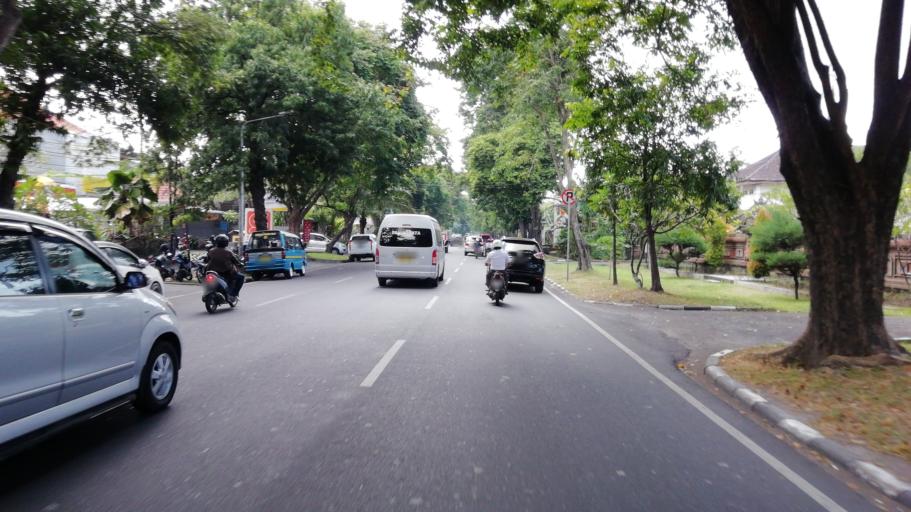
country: ID
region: Bali
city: Denpasar
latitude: -8.6670
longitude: 115.2258
